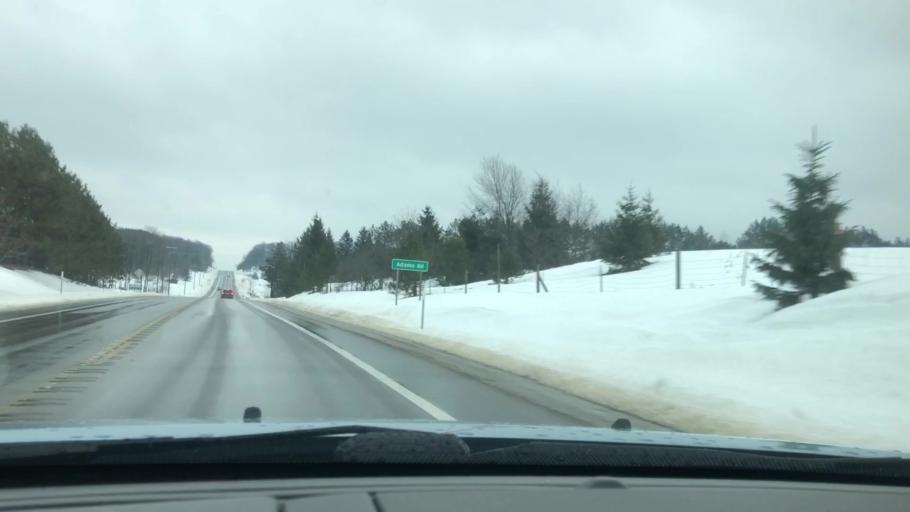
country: US
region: Michigan
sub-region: Charlevoix County
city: East Jordan
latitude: 45.0962
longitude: -85.0226
